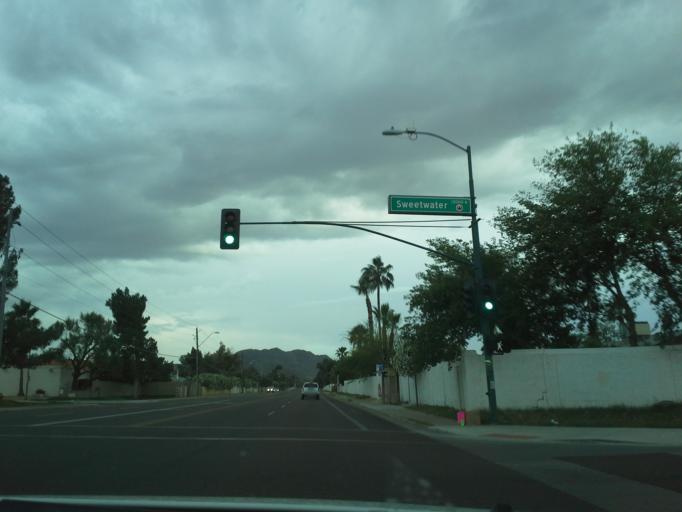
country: US
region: Arizona
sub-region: Maricopa County
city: Paradise Valley
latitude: 33.6045
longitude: -111.9960
